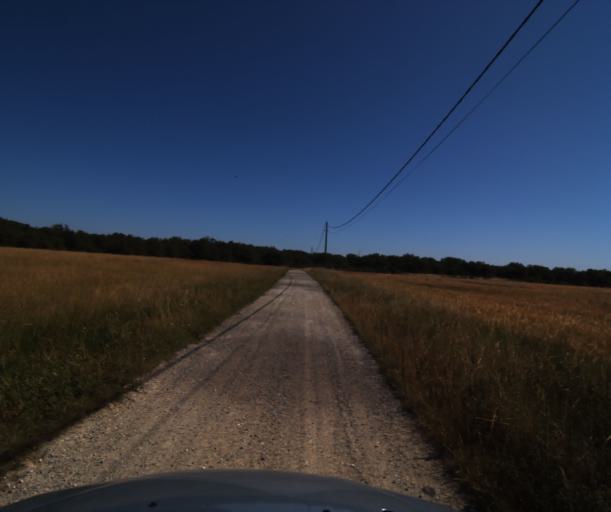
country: FR
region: Midi-Pyrenees
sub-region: Departement de la Haute-Garonne
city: Eaunes
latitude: 43.4204
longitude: 1.3245
